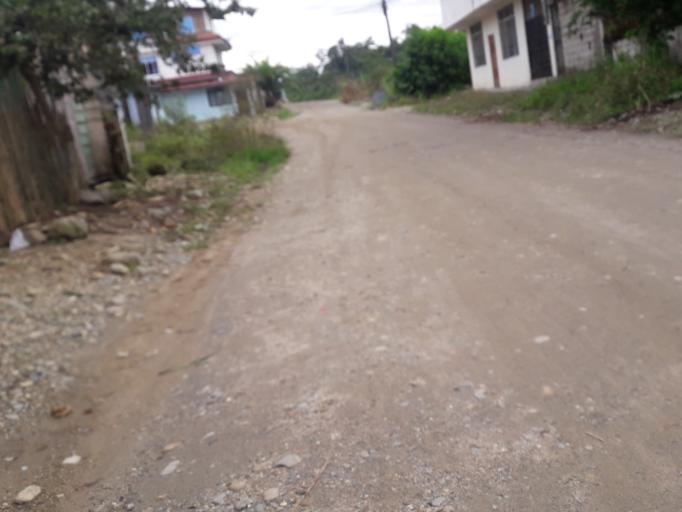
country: EC
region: Napo
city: Tena
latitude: -0.9846
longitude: -77.8182
